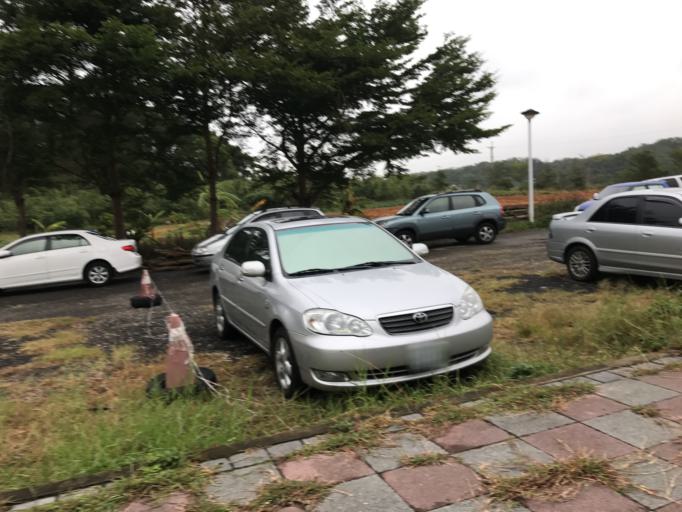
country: TW
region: Taiwan
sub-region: Hsinchu
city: Hsinchu
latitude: 24.7563
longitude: 120.9533
